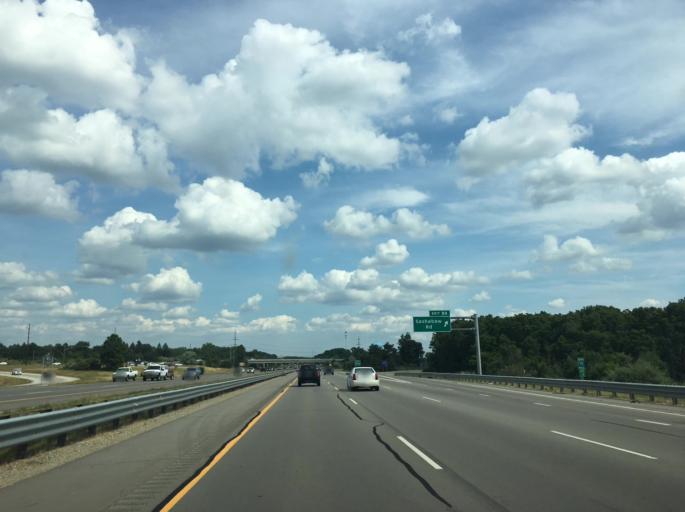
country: US
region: Michigan
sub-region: Oakland County
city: Clarkston
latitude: 42.7389
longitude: -83.3845
